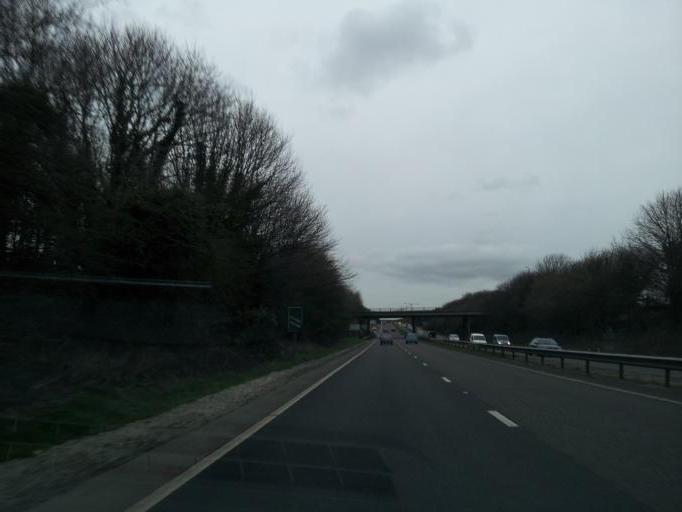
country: GB
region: England
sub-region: Cornwall
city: St. Day
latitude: 50.2550
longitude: -5.1984
